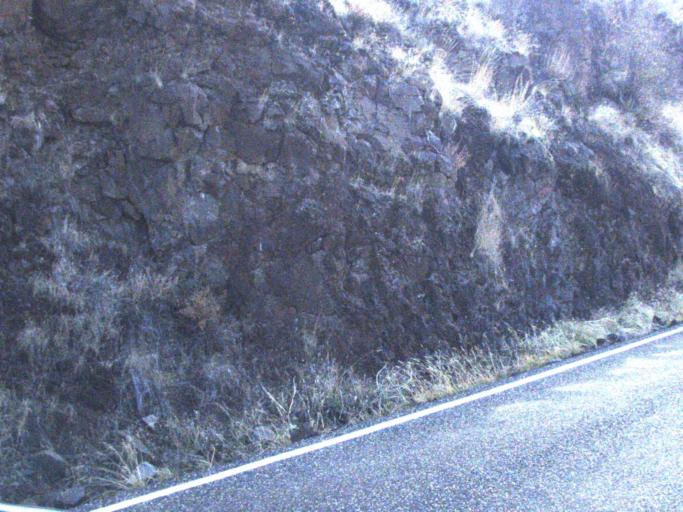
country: US
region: Washington
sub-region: Asotin County
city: Asotin
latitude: 46.0017
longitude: -117.2787
